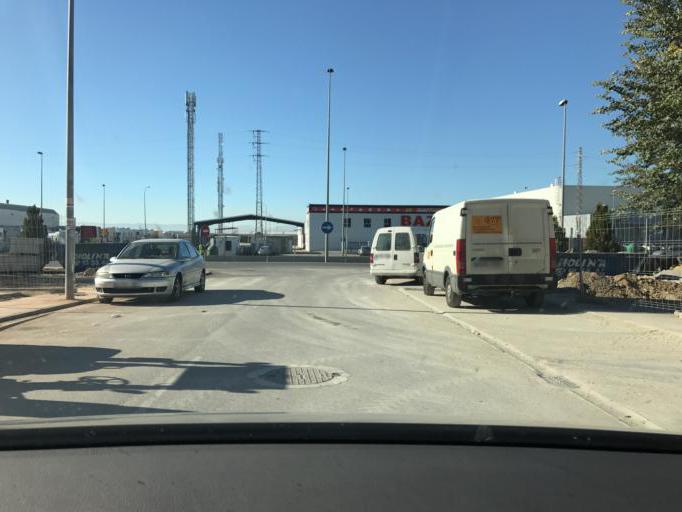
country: ES
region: Andalusia
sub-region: Provincia de Granada
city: Peligros
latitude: 37.2277
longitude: -3.6356
